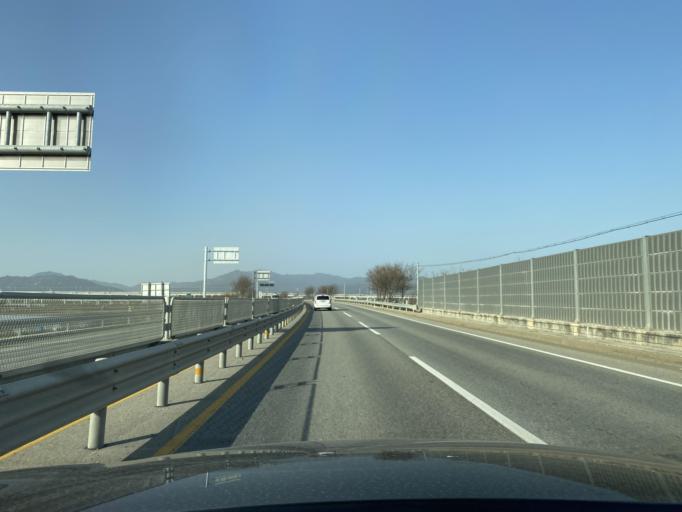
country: KR
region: Chungcheongnam-do
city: Yesan
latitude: 36.6919
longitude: 126.7335
